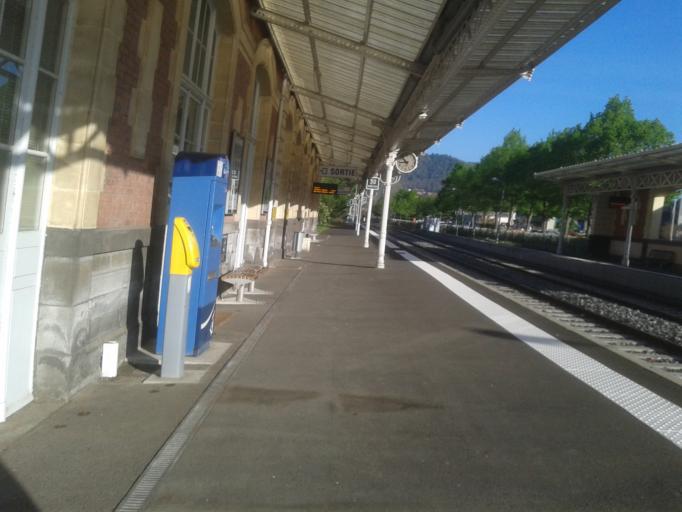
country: FR
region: Auvergne
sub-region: Departement du Puy-de-Dome
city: Chamalieres
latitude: 45.7676
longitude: 3.0619
